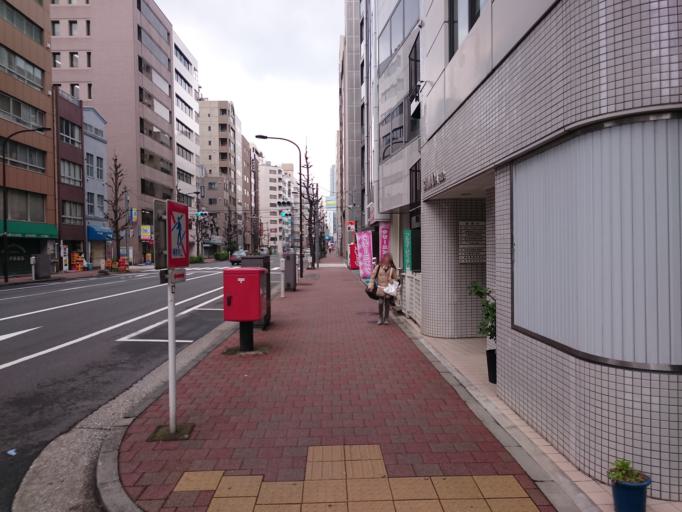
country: JP
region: Tokyo
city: Tokyo
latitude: 35.6931
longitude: 139.7771
